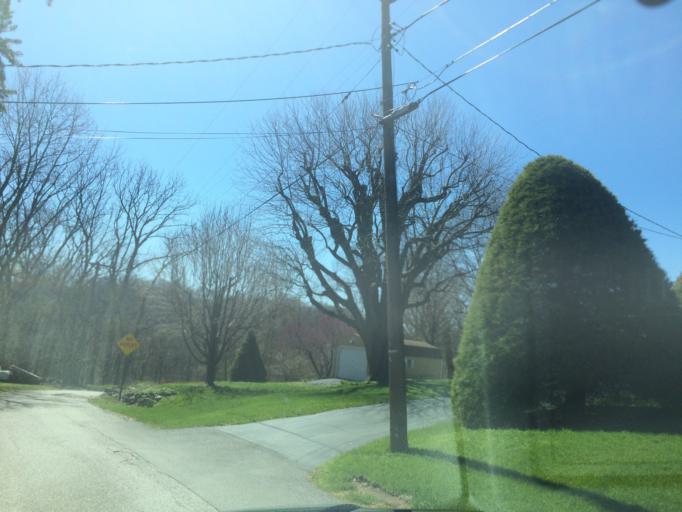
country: US
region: Maryland
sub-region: Carroll County
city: Westminster
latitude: 39.5684
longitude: -77.0008
